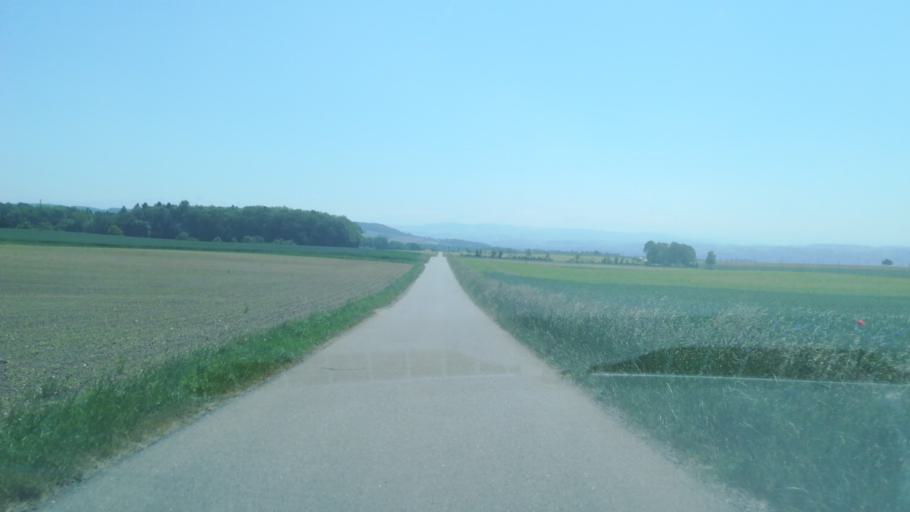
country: CH
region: Thurgau
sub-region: Kreuzlingen District
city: Ermatingen
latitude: 47.6339
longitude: 9.0769
